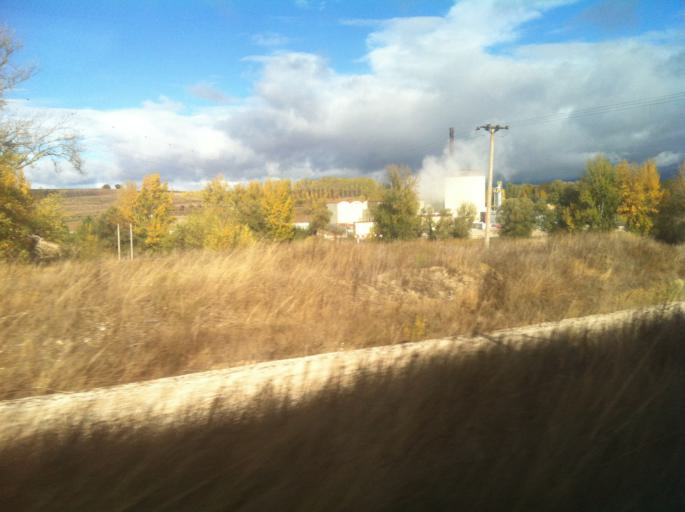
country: ES
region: Castille and Leon
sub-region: Provincia de Burgos
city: Briviesca
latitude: 42.5719
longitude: -3.3042
